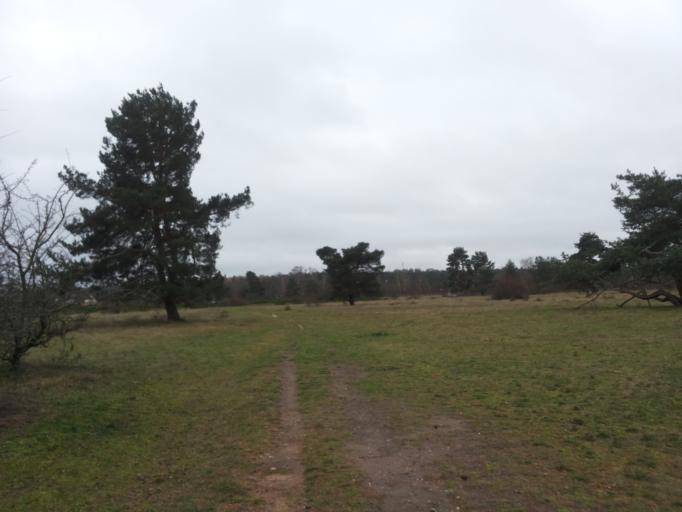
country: DE
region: Bavaria
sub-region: Regierungsbezirk Mittelfranken
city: Wendelstein
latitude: 49.4012
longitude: 11.1680
